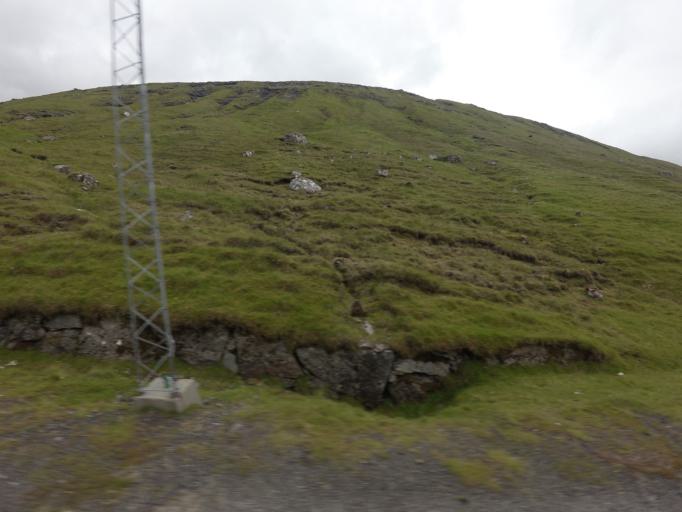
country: FO
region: Streymoy
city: Kollafjordhur
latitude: 62.1278
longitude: -7.0080
